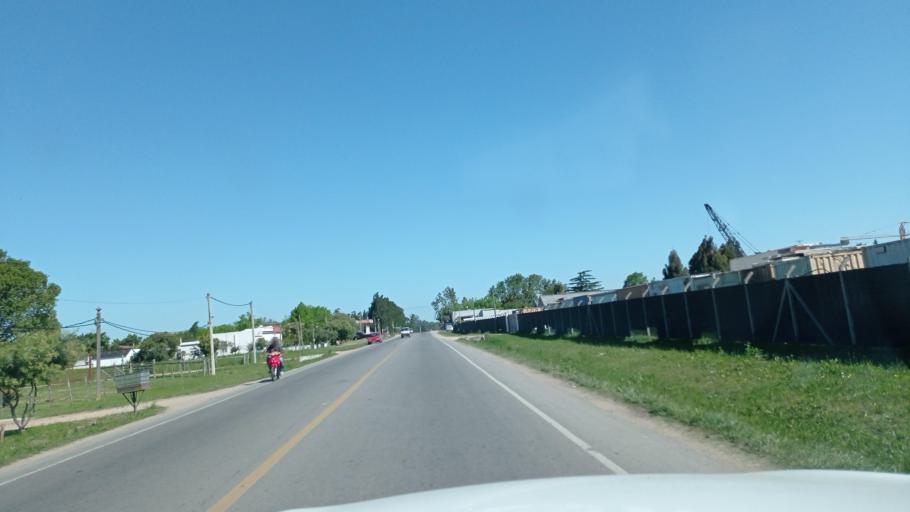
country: UY
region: Canelones
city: La Paz
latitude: -34.7883
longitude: -56.1661
